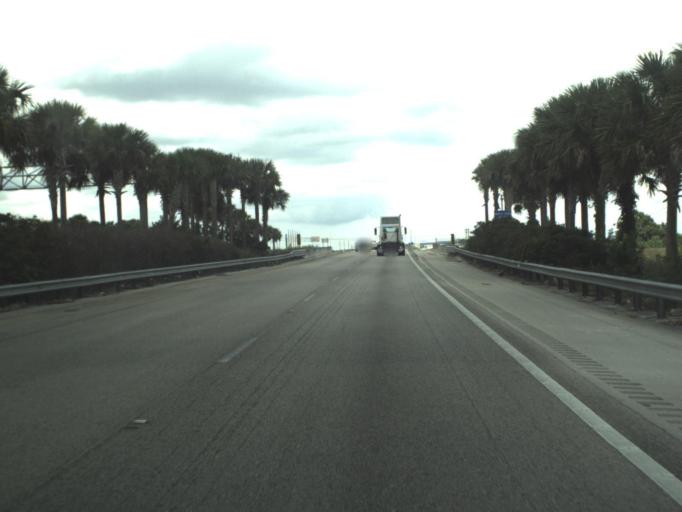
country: US
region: Florida
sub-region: Broward County
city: Weston
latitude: 26.1458
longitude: -80.4623
